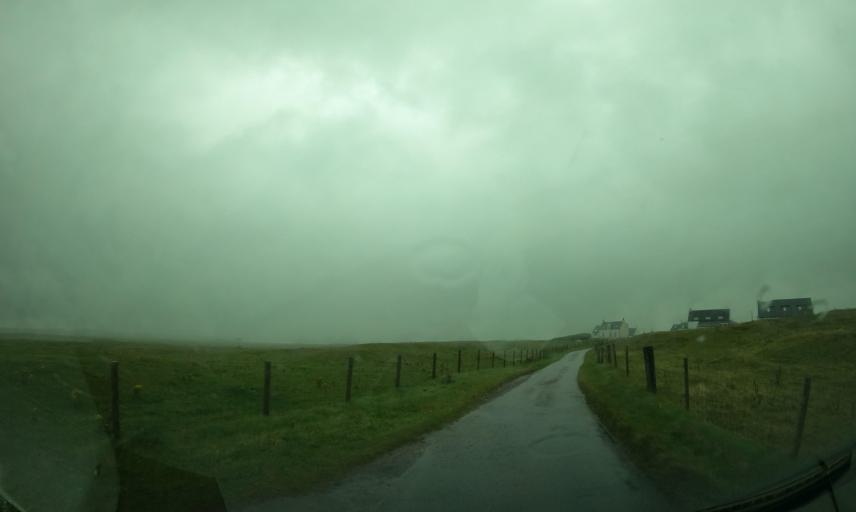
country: GB
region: Scotland
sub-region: Eilean Siar
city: Barra
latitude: 56.4568
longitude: -6.9399
